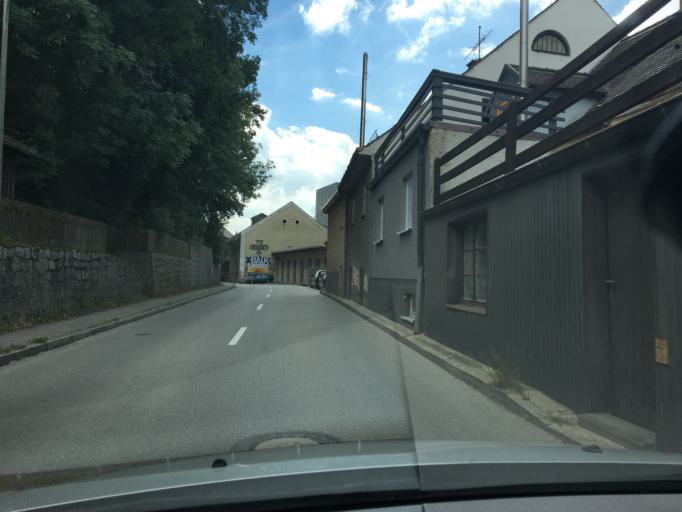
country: DE
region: Bavaria
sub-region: Lower Bavaria
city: Vilsbiburg
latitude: 48.4464
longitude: 12.3560
